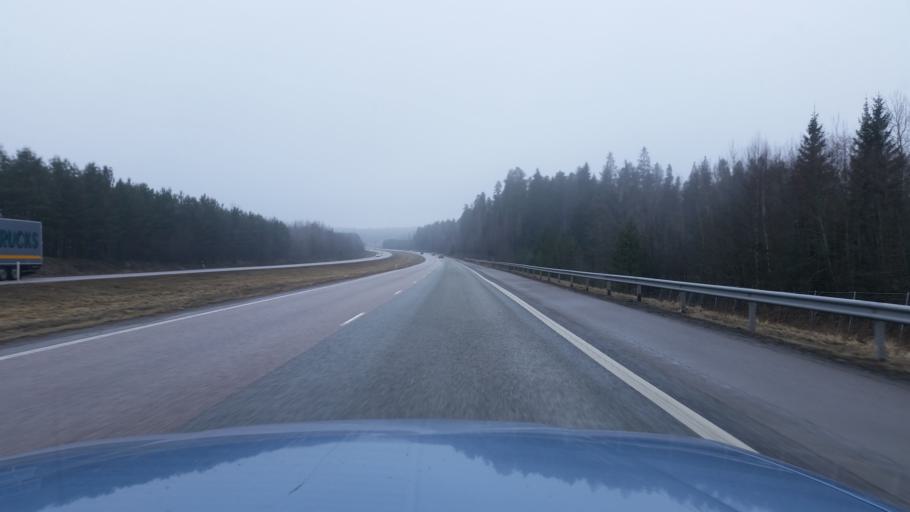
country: FI
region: Uusimaa
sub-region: Helsinki
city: Nurmijaervi
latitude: 60.4365
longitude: 24.8329
